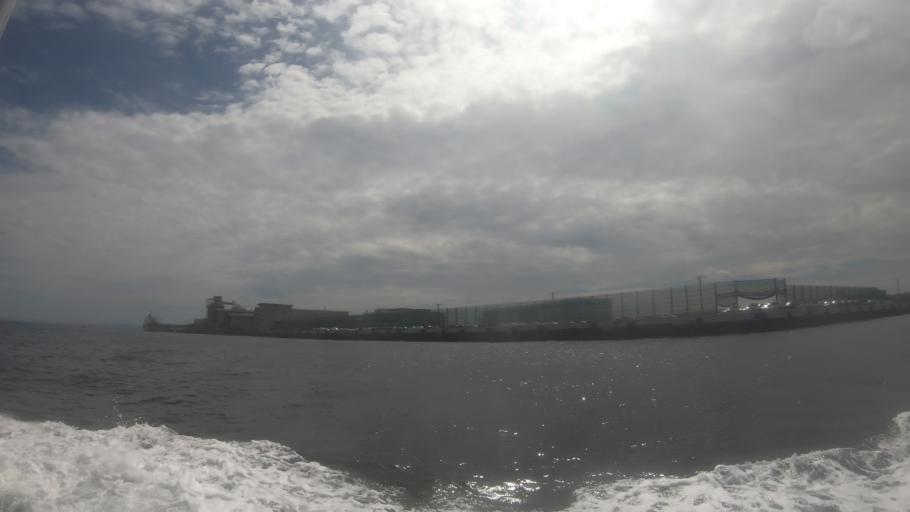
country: JP
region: Kanagawa
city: Yokohama
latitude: 35.3915
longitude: 139.6453
